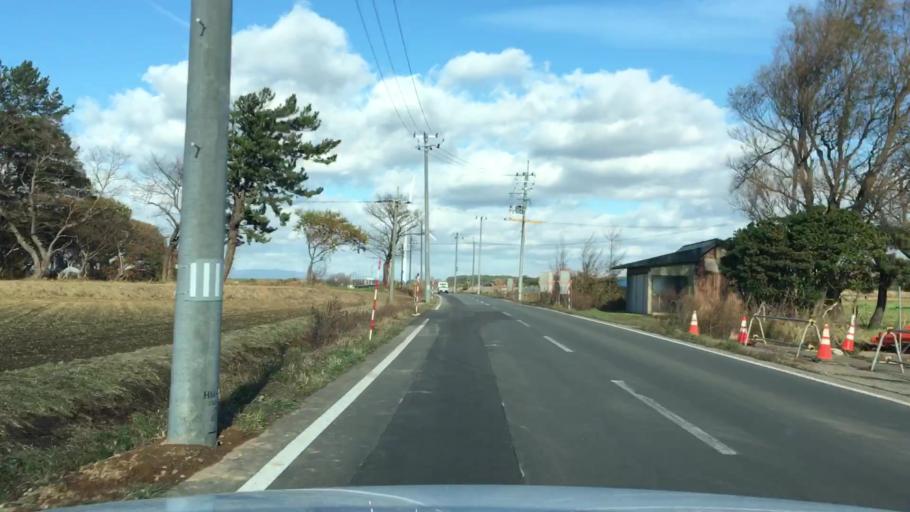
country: JP
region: Aomori
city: Shimokizukuri
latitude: 40.8556
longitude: 140.3024
